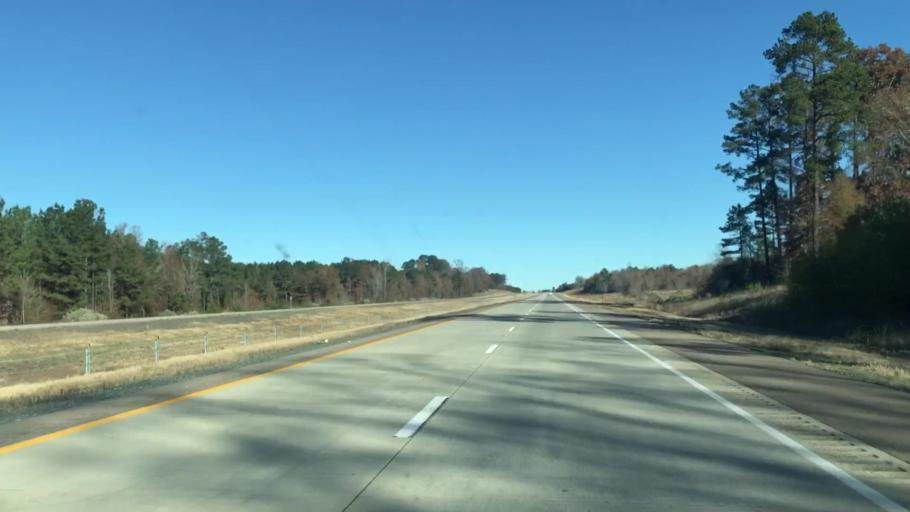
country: US
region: Louisiana
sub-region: Caddo Parish
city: Vivian
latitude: 33.0330
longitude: -93.9007
